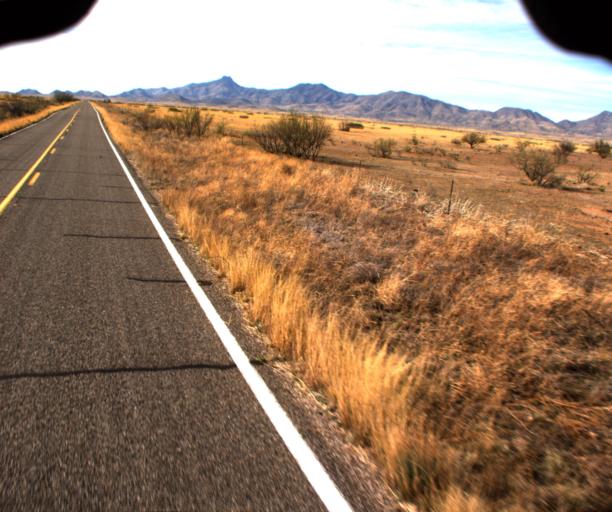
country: US
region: Arizona
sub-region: Cochise County
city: Willcox
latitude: 32.0841
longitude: -109.5248
